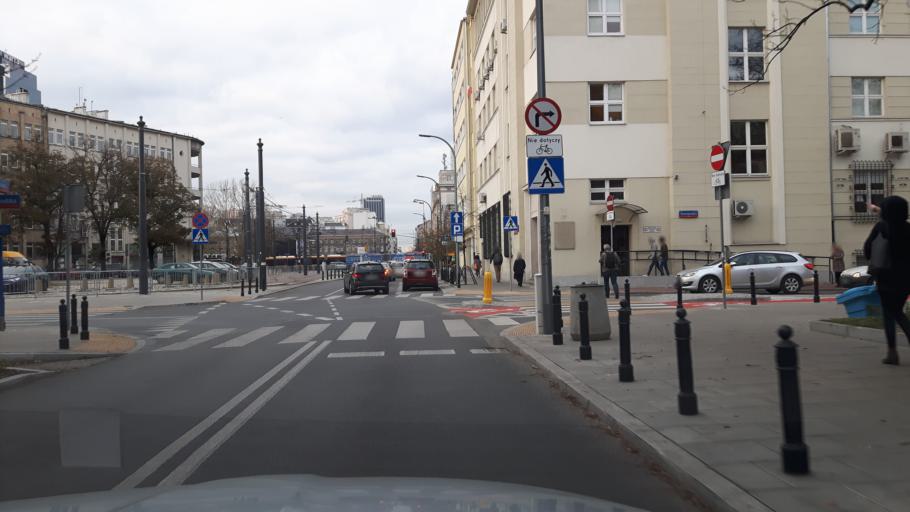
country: PL
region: Masovian Voivodeship
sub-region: Warszawa
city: Ochota
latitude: 52.2252
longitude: 20.9967
